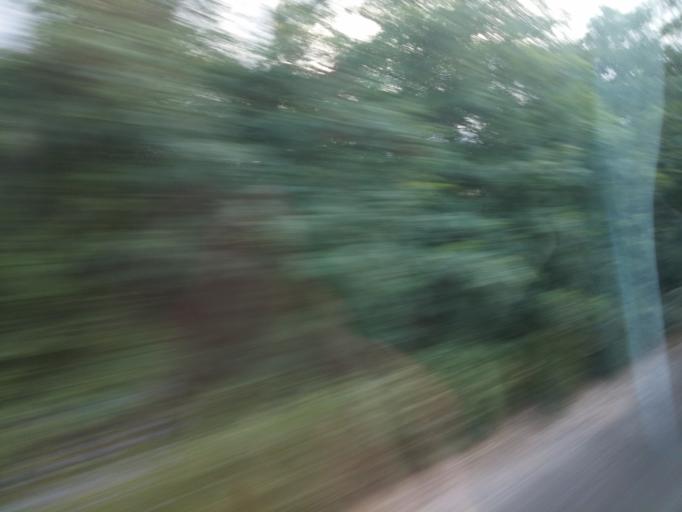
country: HU
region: Veszprem
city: Varpalota
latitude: 47.2190
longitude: 18.1493
